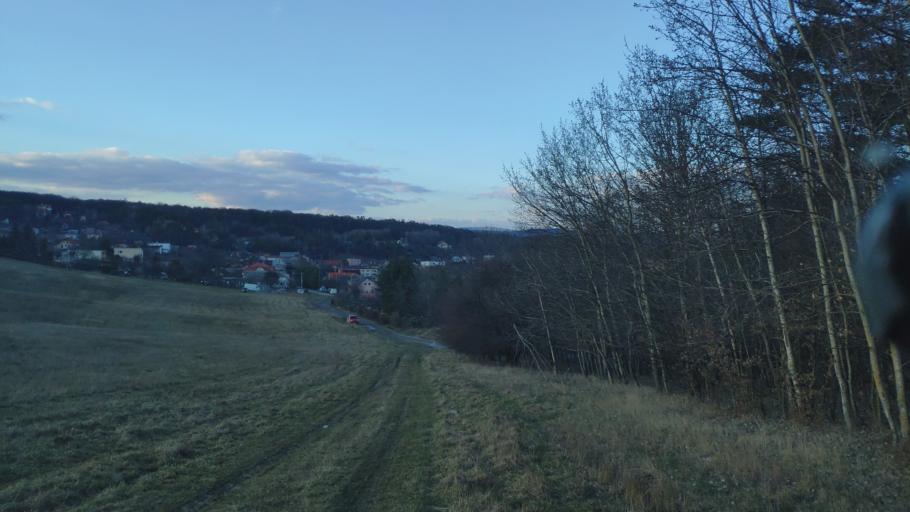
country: SK
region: Kosicky
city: Kosice
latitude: 48.7010
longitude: 21.1809
